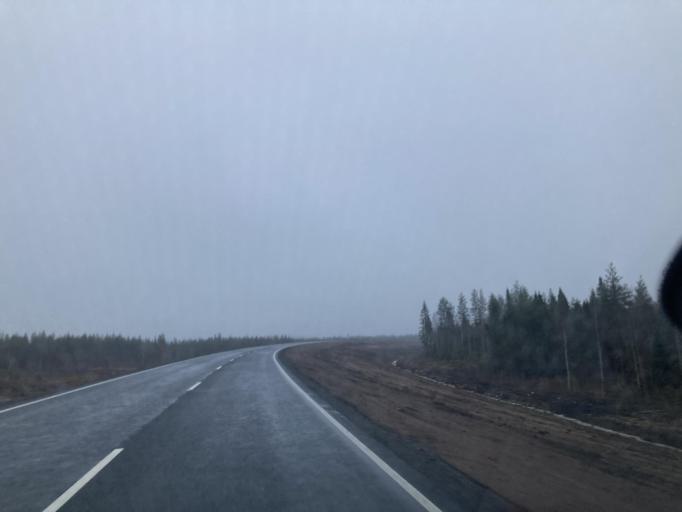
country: FI
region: Lapland
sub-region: Rovaniemi
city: Rovaniemi
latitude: 66.5890
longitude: 25.7997
